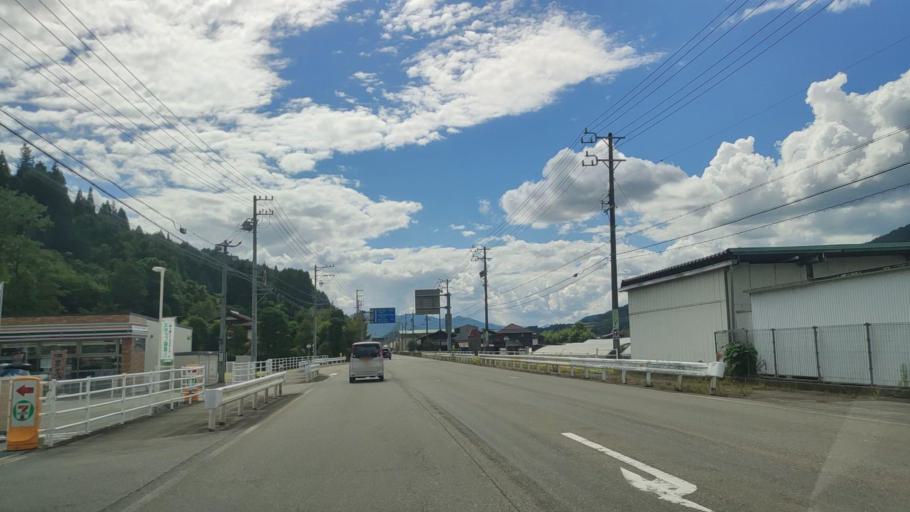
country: JP
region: Gifu
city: Takayama
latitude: 36.1858
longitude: 137.2540
